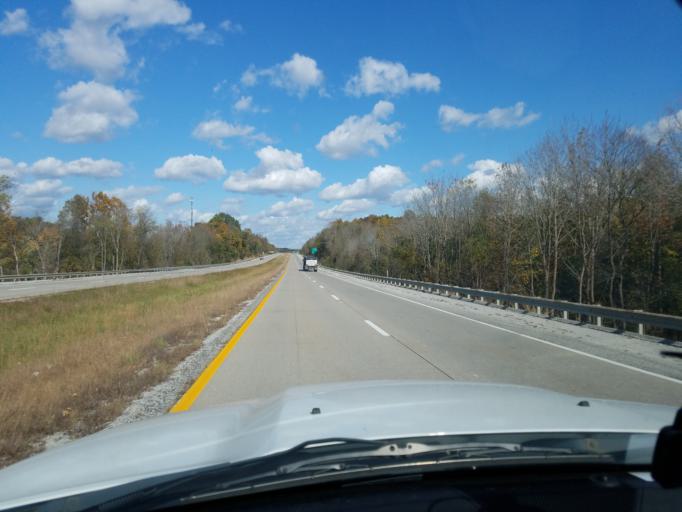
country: US
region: Kentucky
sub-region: Ohio County
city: Oak Grove
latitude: 37.2872
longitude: -86.7422
